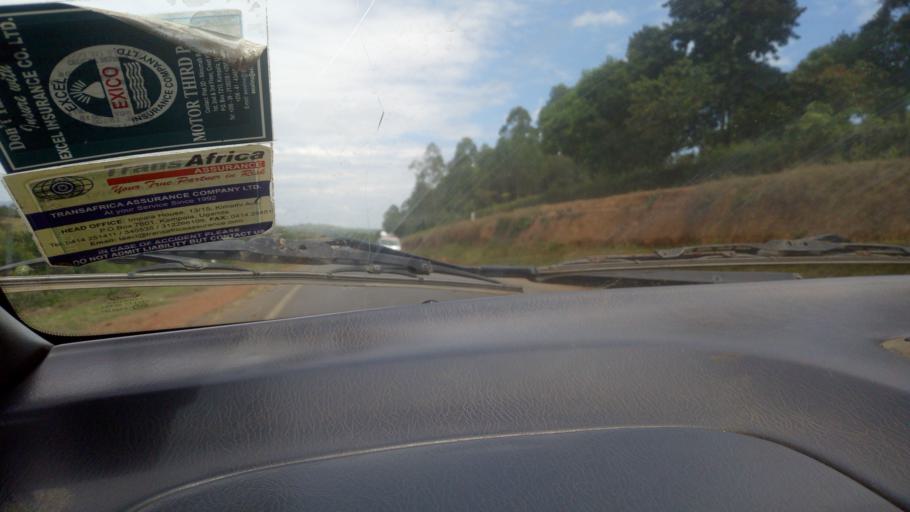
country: UG
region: Western Region
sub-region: Mbarara District
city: Bwizibwera
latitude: -0.3868
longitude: 30.5654
